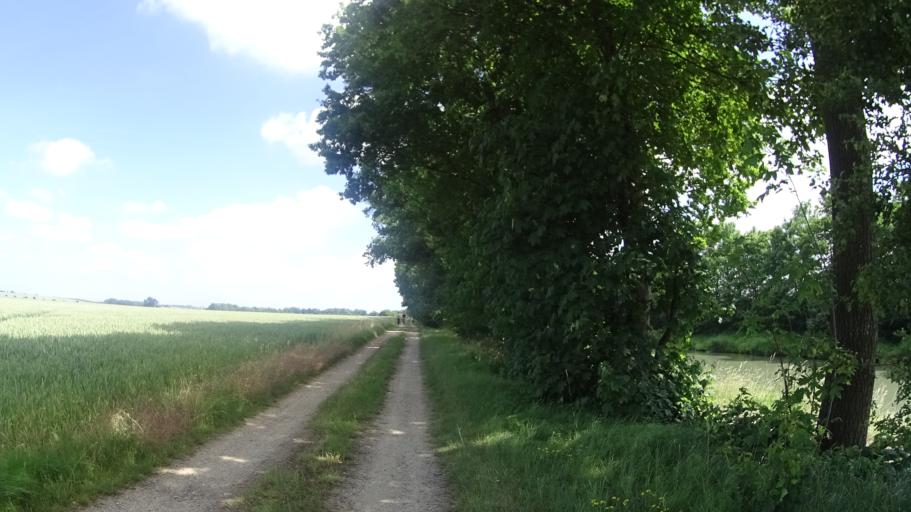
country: DE
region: Lower Saxony
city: Algermissen
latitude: 52.2403
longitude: 9.9465
